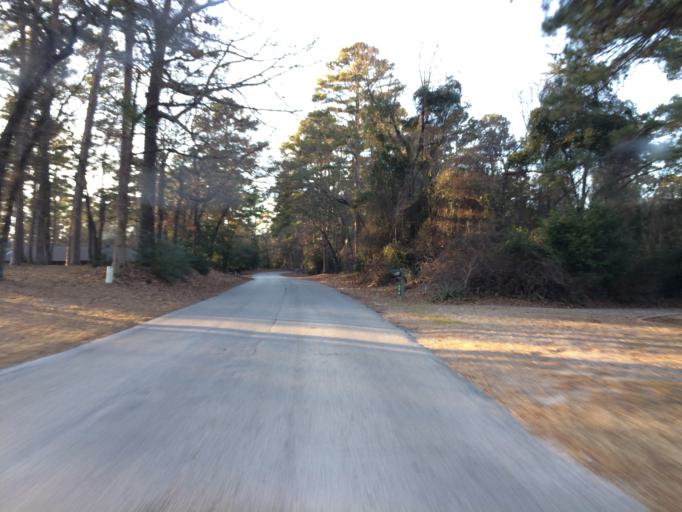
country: US
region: Texas
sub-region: Wood County
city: Hawkins
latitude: 32.7199
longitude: -95.1941
